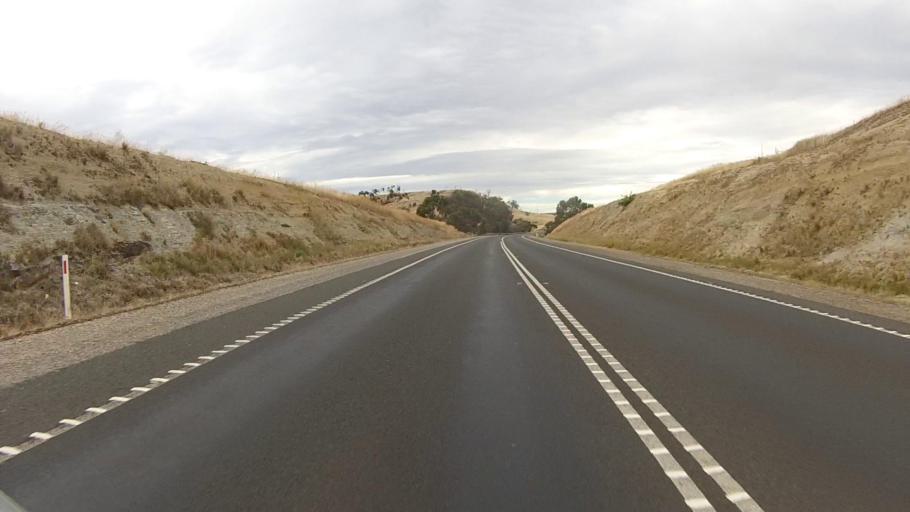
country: AU
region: Tasmania
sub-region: Brighton
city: Bridgewater
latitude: -42.3462
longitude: 147.3379
